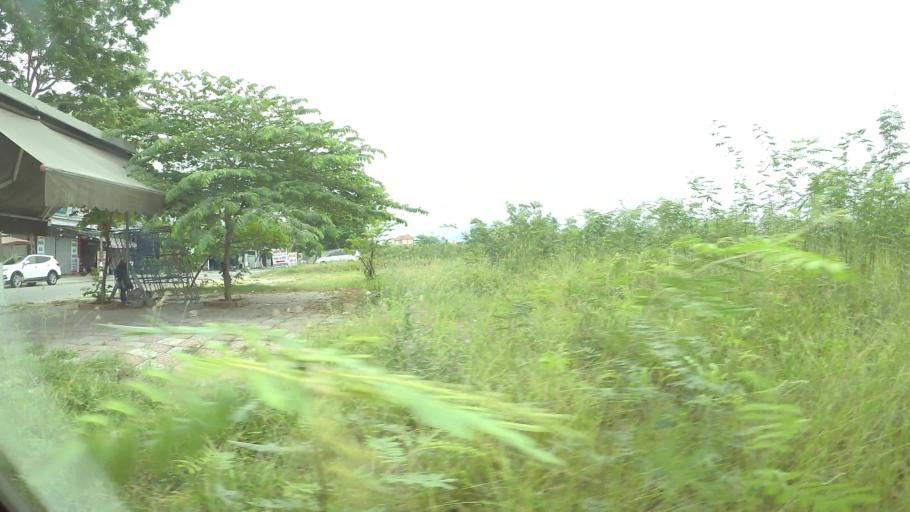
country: VN
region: Da Nang
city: Lien Chieu
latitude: 16.0764
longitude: 108.1593
